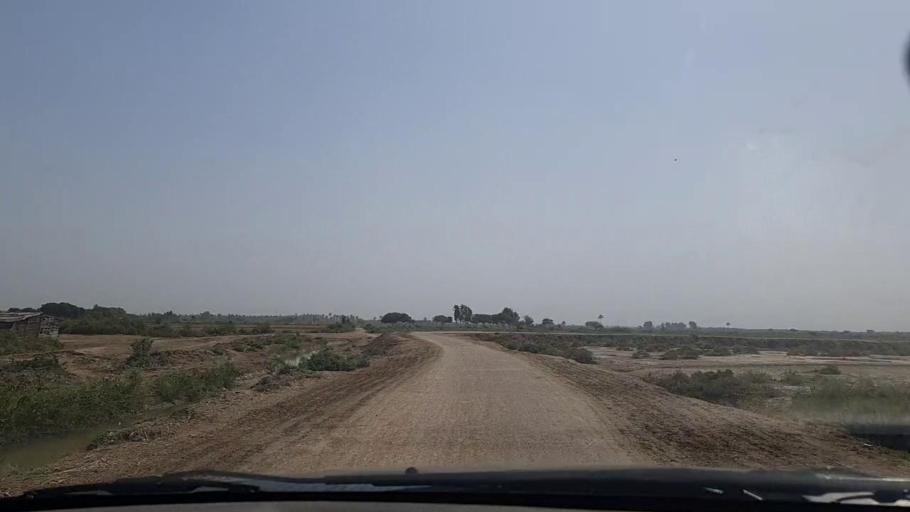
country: PK
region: Sindh
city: Keti Bandar
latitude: 24.2695
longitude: 67.6729
